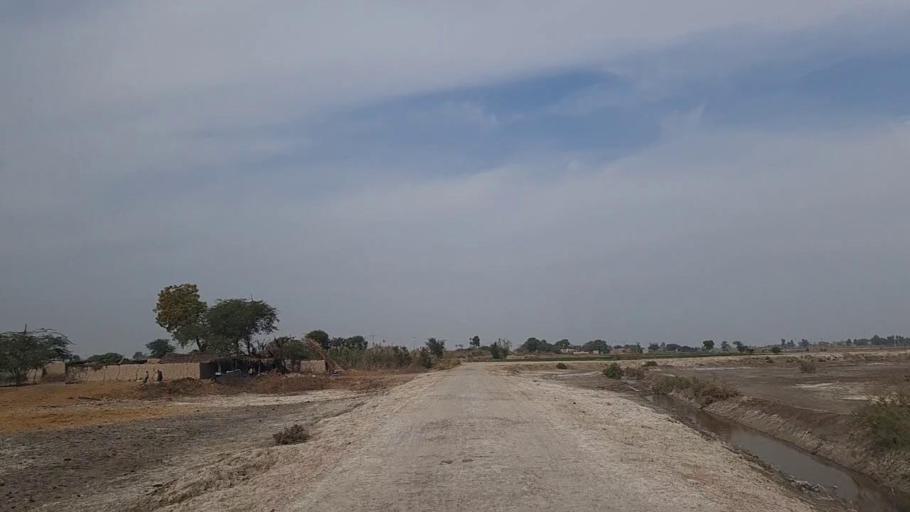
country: PK
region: Sindh
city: Daur
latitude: 26.4773
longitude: 68.4024
